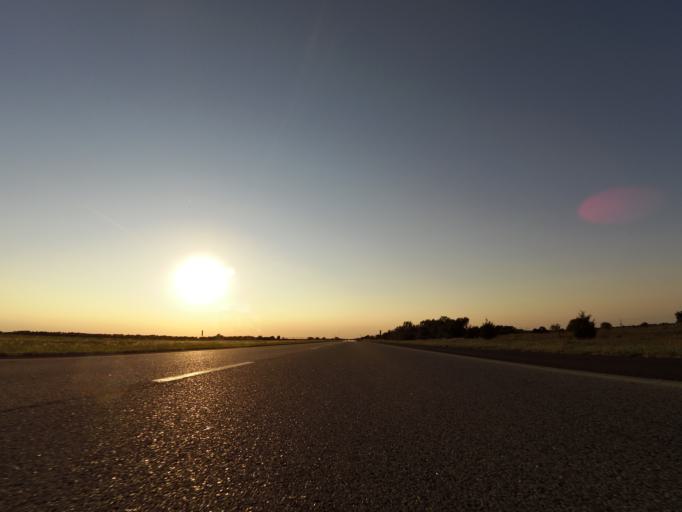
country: US
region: Kansas
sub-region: Reno County
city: South Hutchinson
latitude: 37.9508
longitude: -97.8931
